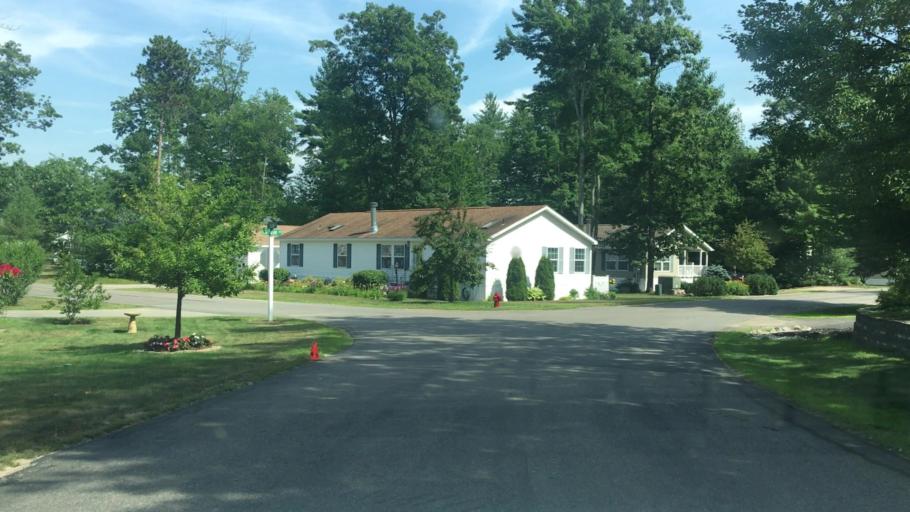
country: US
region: New Hampshire
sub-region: Strafford County
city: Rochester
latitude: 43.3156
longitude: -70.9240
